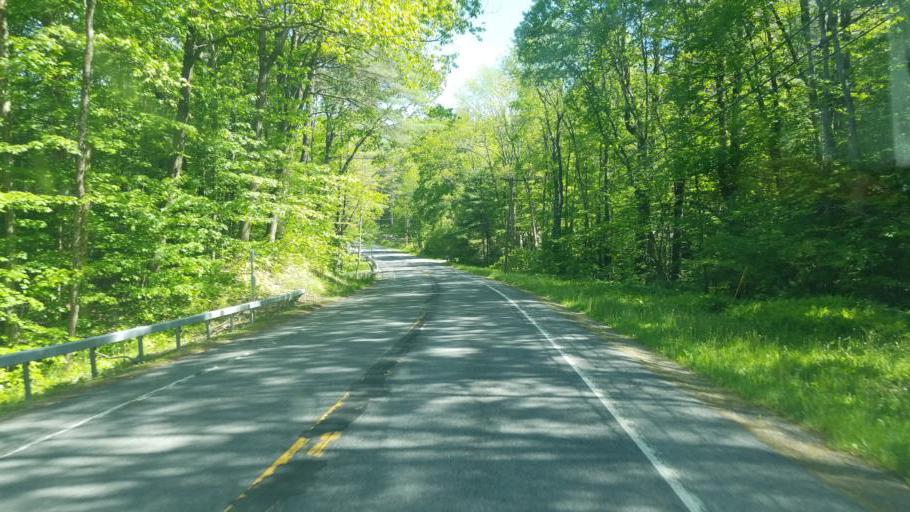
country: US
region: New York
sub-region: Fulton County
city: Johnstown
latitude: 43.0898
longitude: -74.5031
